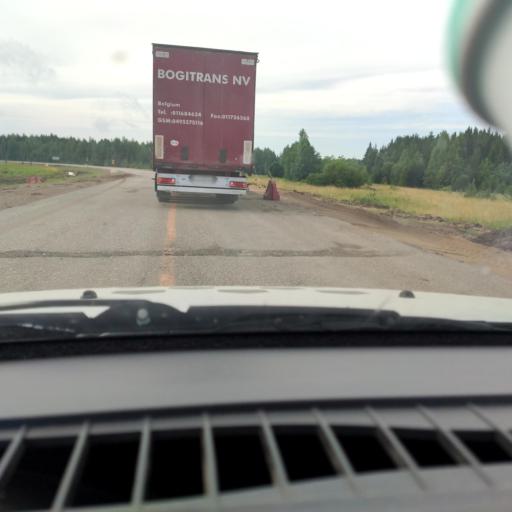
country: RU
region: Kirov
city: Kostino
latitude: 58.8251
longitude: 53.3107
